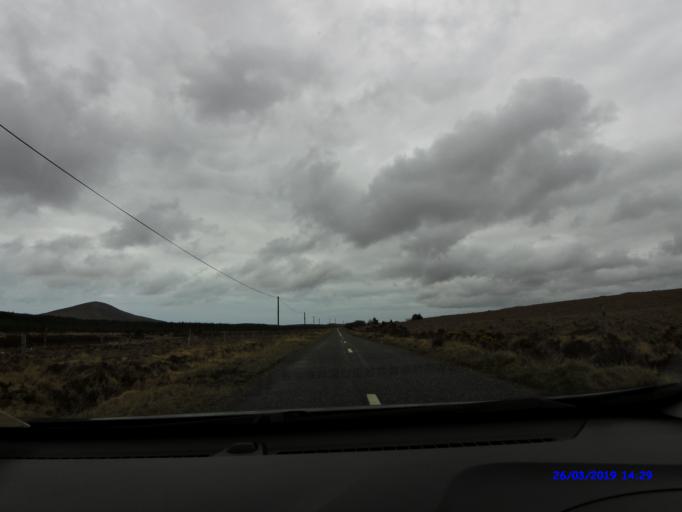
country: IE
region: Connaught
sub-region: Maigh Eo
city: Crossmolina
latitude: 54.2615
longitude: -9.6095
